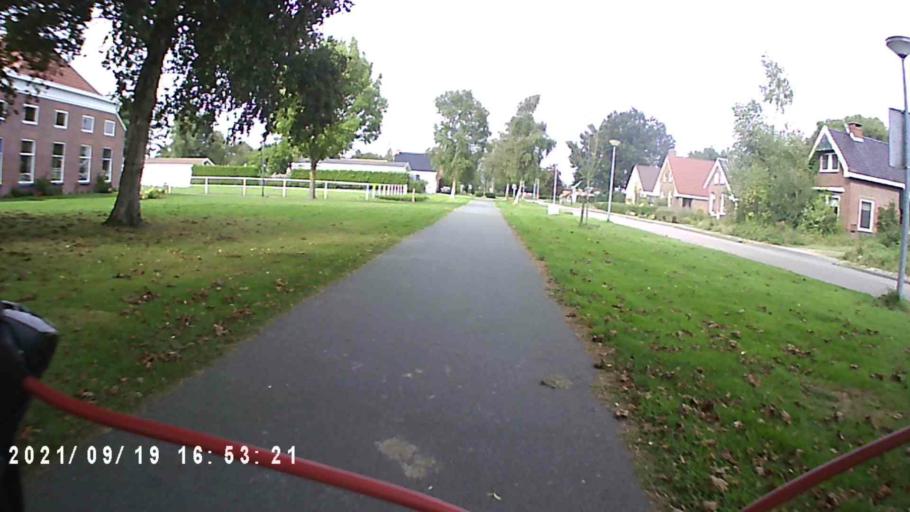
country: NL
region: Groningen
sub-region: Gemeente  Oldambt
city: Winschoten
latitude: 53.1835
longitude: 7.0782
